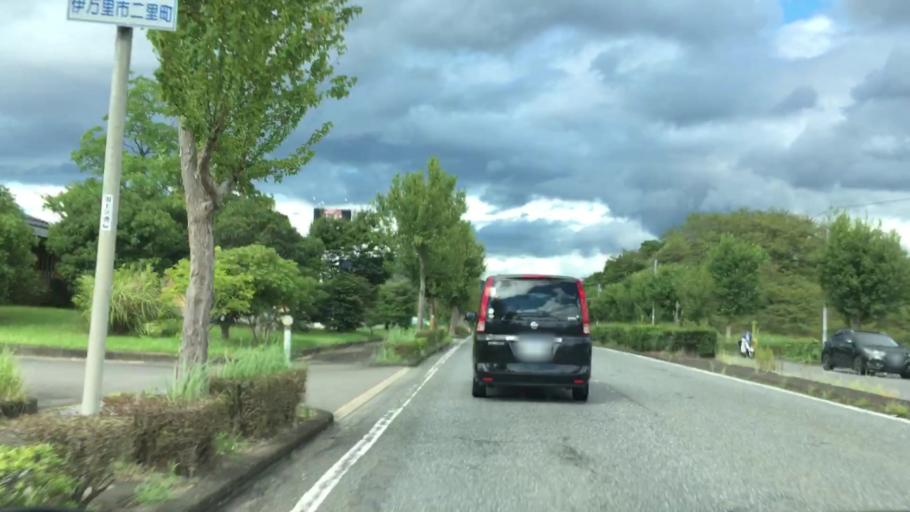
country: JP
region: Saga Prefecture
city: Imaricho-ko
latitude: 33.2658
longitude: 129.8651
